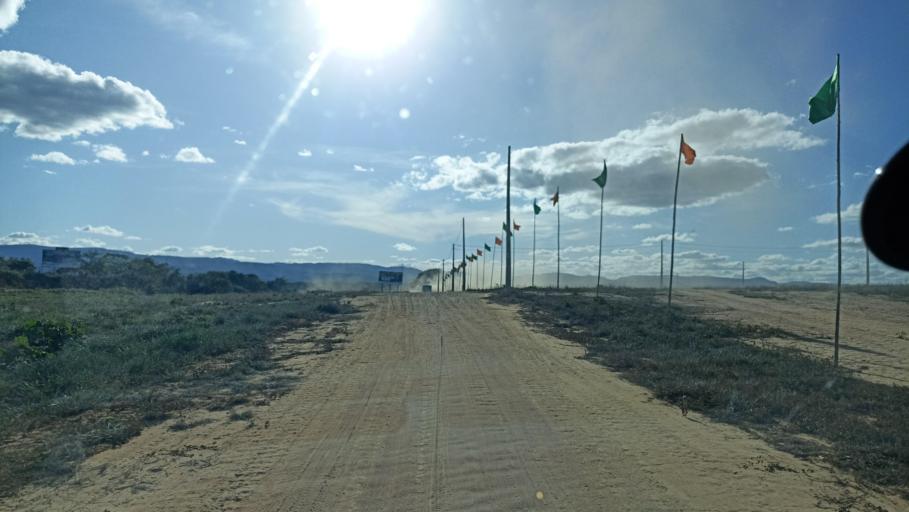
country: BR
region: Bahia
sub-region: Andarai
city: Vera Cruz
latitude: -12.4953
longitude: -41.3004
